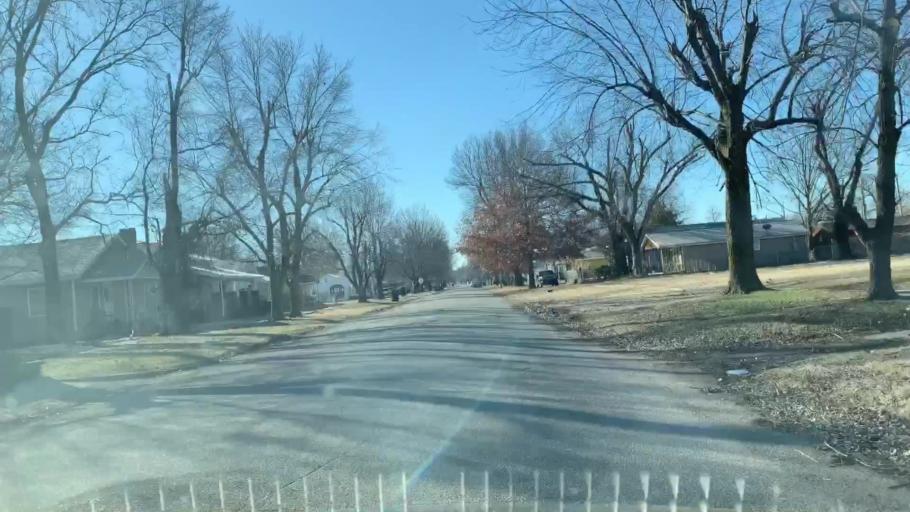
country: US
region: Kansas
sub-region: Cherokee County
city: Baxter Springs
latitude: 37.0204
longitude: -94.7343
